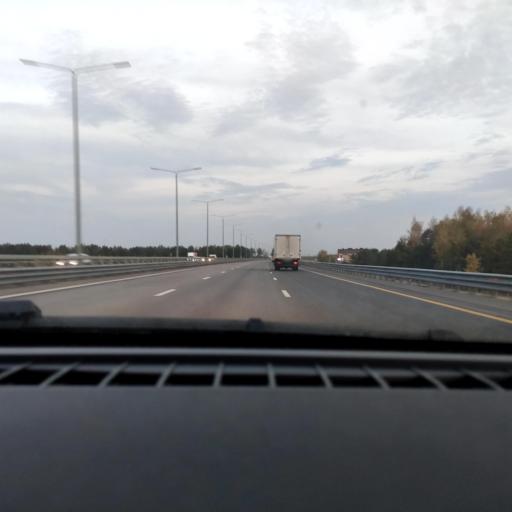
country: RU
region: Voronezj
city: Somovo
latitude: 51.7835
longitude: 39.2920
